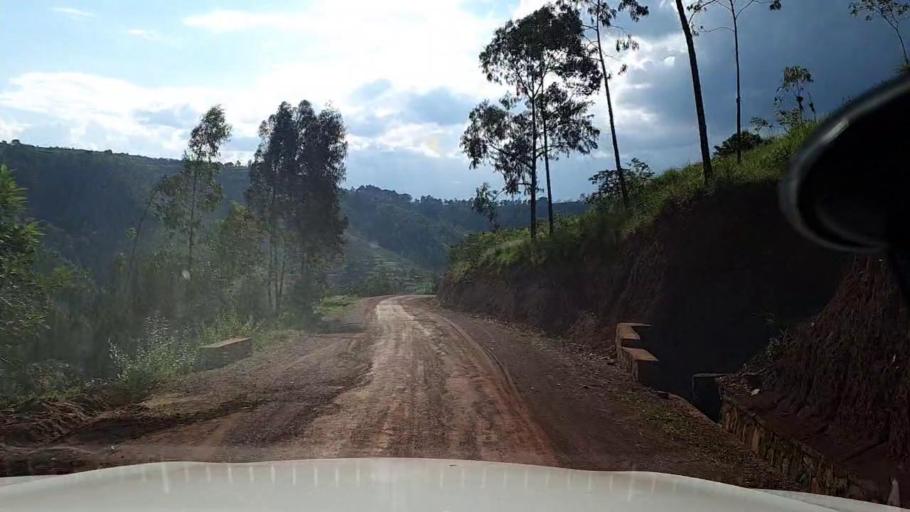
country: RW
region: Kigali
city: Kigali
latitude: -1.8447
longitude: 29.8596
